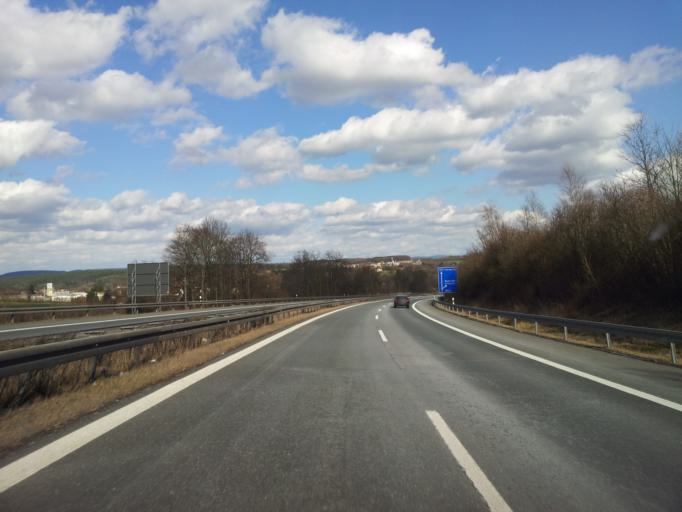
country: DE
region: Bavaria
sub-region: Upper Franconia
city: Thurnau
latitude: 50.0165
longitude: 11.3793
